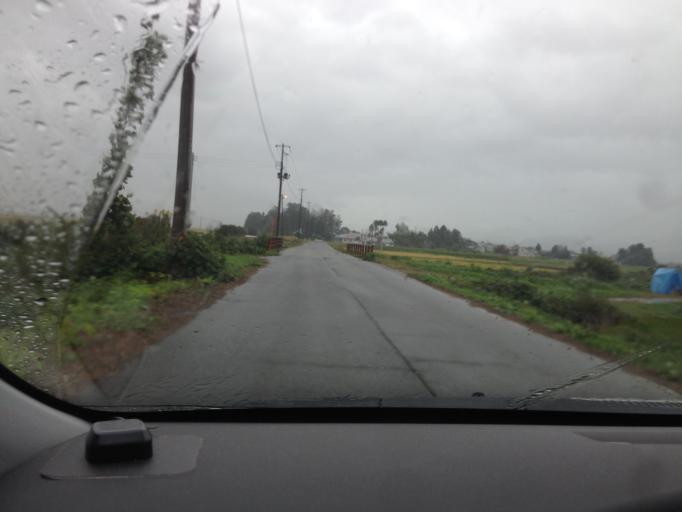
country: JP
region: Fukushima
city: Kitakata
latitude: 37.4811
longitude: 139.8266
